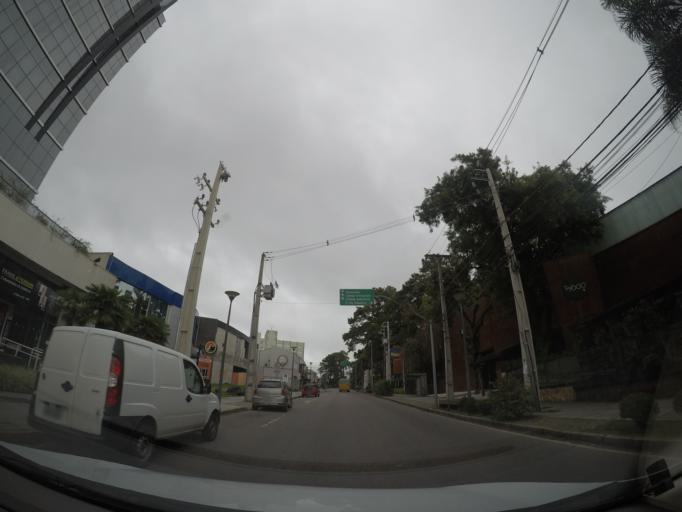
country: BR
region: Parana
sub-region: Curitiba
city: Curitiba
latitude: -25.4446
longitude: -49.2928
